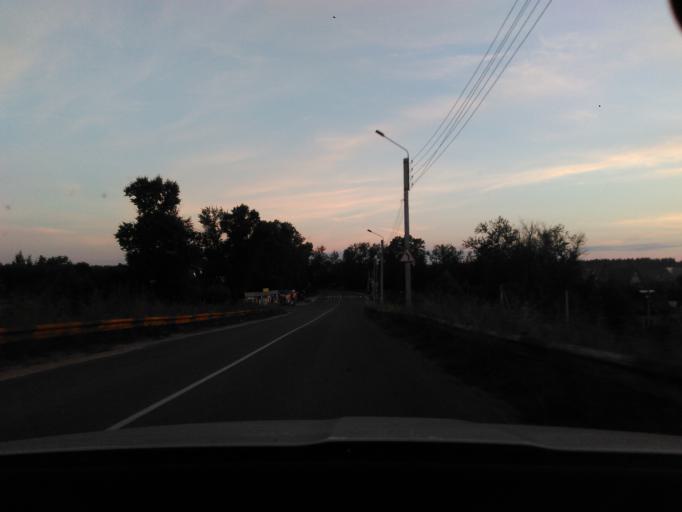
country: RU
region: Moskovskaya
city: Klin
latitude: 56.2677
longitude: 36.7596
